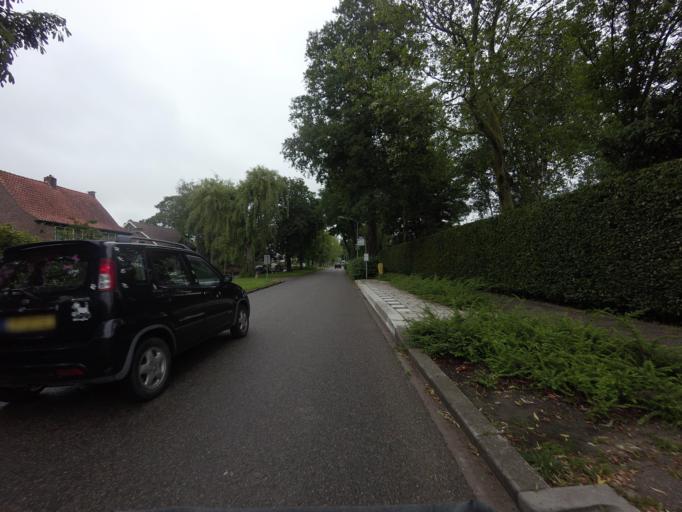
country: NL
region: North Holland
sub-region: Gemeente Opmeer
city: Opmeer
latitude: 52.7572
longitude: 4.8996
